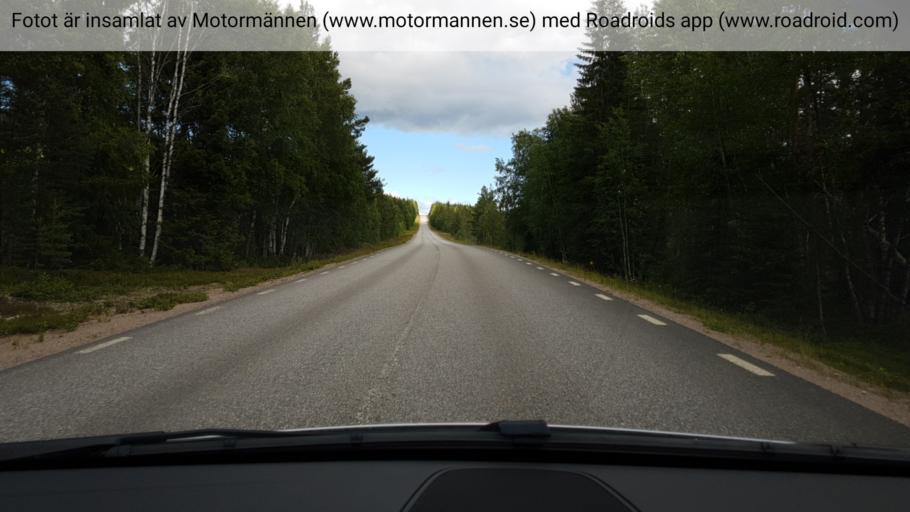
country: SE
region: Jaemtland
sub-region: Harjedalens Kommun
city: Sveg
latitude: 62.0006
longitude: 14.9233
